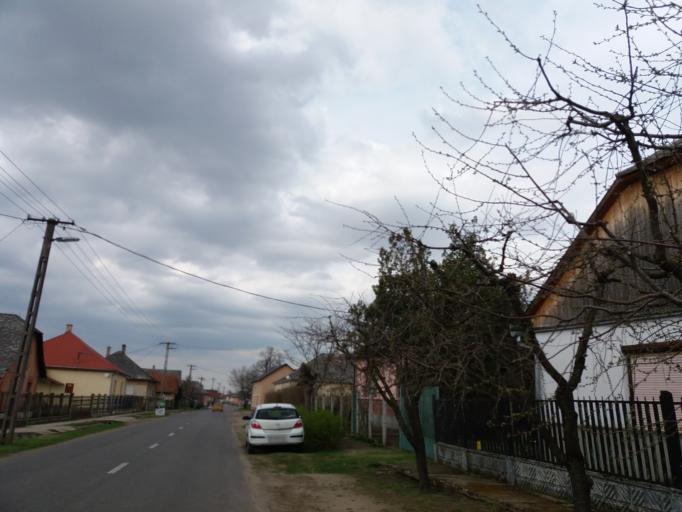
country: HU
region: Szabolcs-Szatmar-Bereg
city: Nyirtass
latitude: 48.1138
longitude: 22.0217
